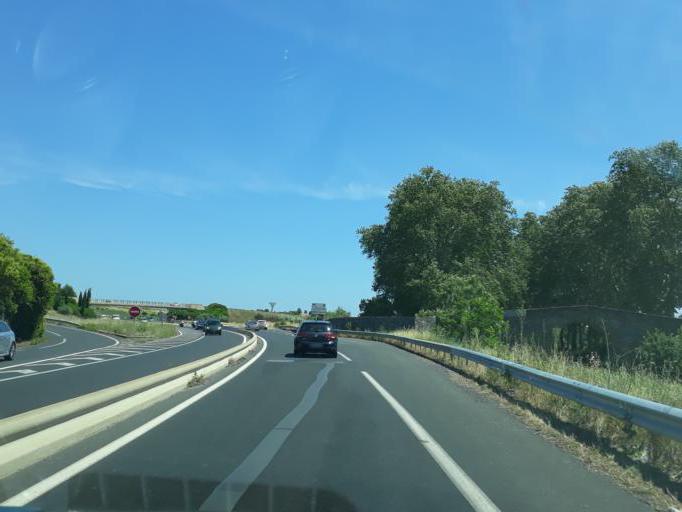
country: FR
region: Languedoc-Roussillon
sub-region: Departement de l'Herault
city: Cers
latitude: 43.3152
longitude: 3.3124
